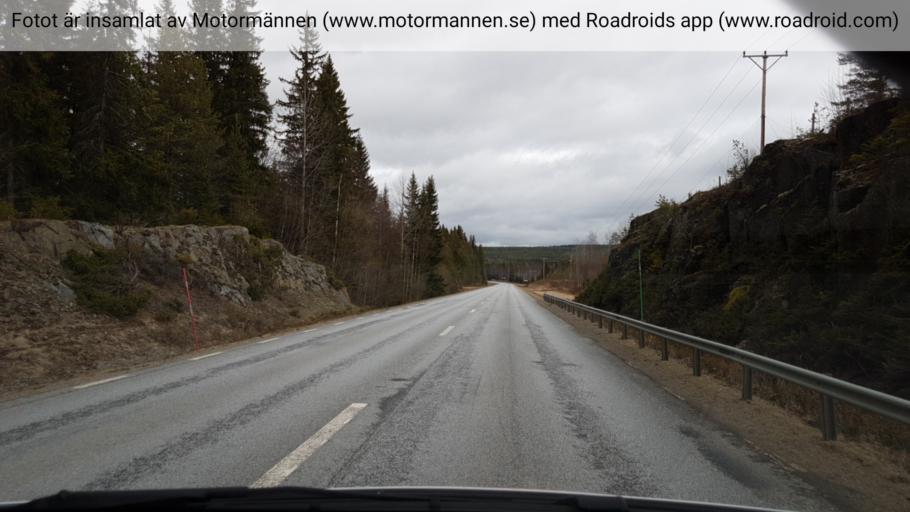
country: SE
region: Vaesterbotten
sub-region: Bjurholms Kommun
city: Bjurholm
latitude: 63.9296
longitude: 19.2766
